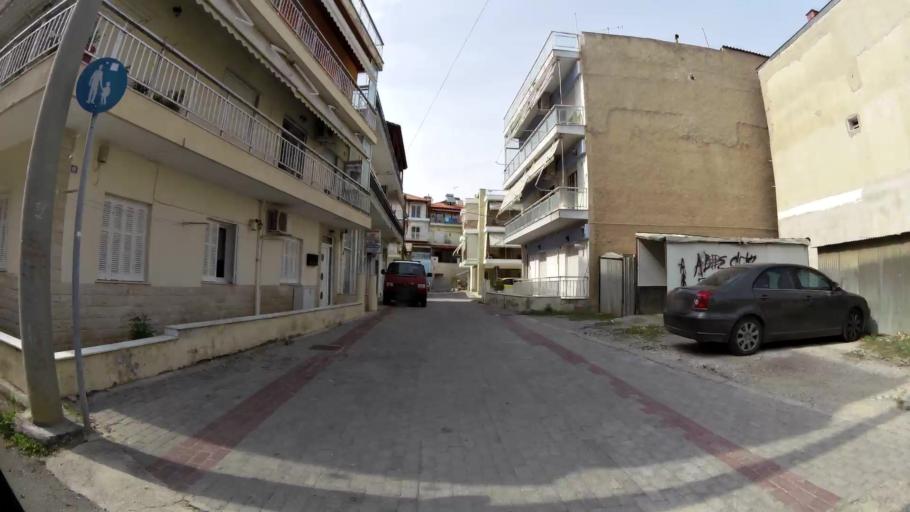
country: GR
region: Central Macedonia
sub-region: Nomos Thessalonikis
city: Stavroupoli
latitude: 40.6808
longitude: 22.9358
